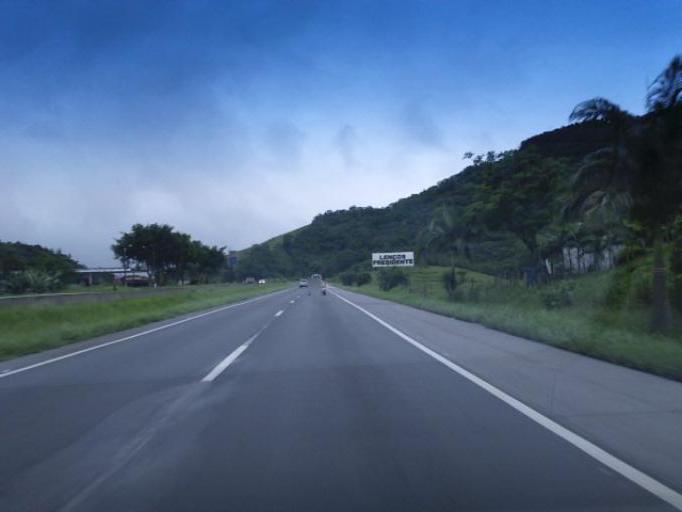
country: BR
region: Sao Paulo
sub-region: Miracatu
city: Miracatu
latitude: -24.3041
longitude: -47.4889
